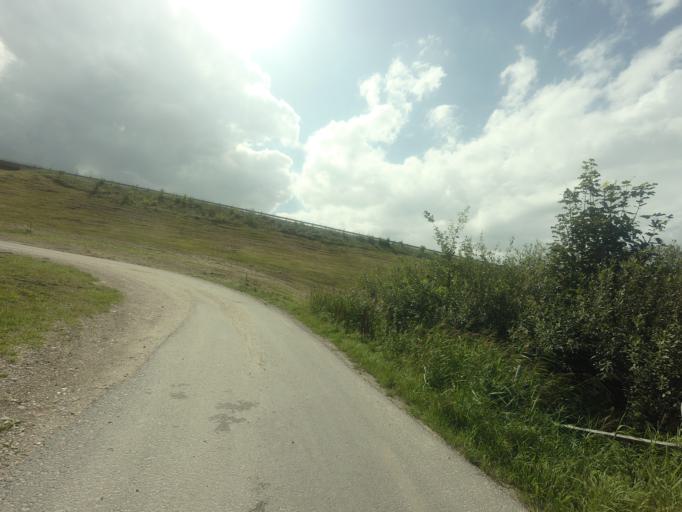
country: NL
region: Friesland
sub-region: Gemeente Skarsterlan
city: Joure
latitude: 52.9750
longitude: 5.7556
